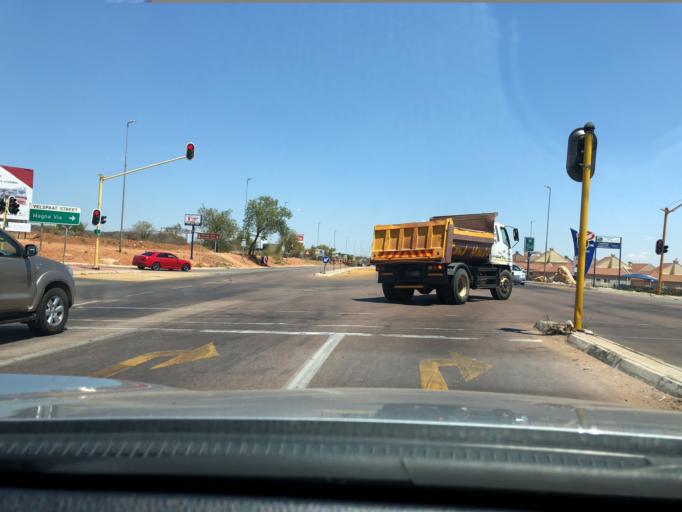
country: ZA
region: Limpopo
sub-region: Capricorn District Municipality
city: Polokwane
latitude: -23.8828
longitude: 29.5001
